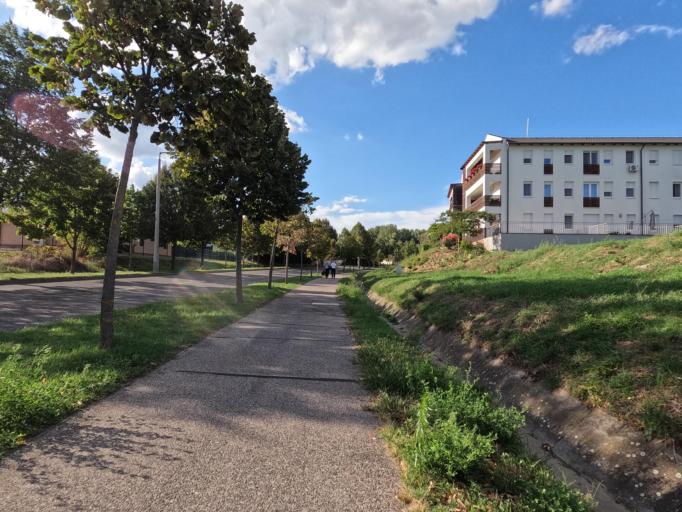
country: HU
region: Tolna
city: Paks
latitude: 46.6117
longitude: 18.8378
